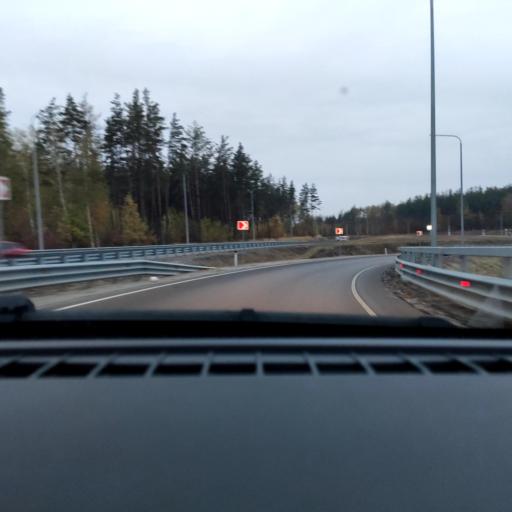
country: RU
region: Voronezj
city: Somovo
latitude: 51.6916
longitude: 39.3054
